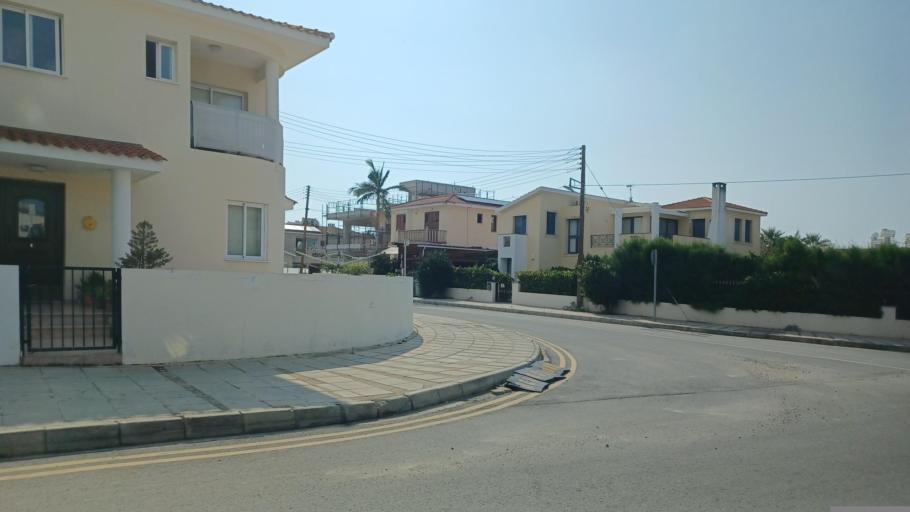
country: CY
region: Pafos
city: Paphos
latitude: 34.7609
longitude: 32.4329
